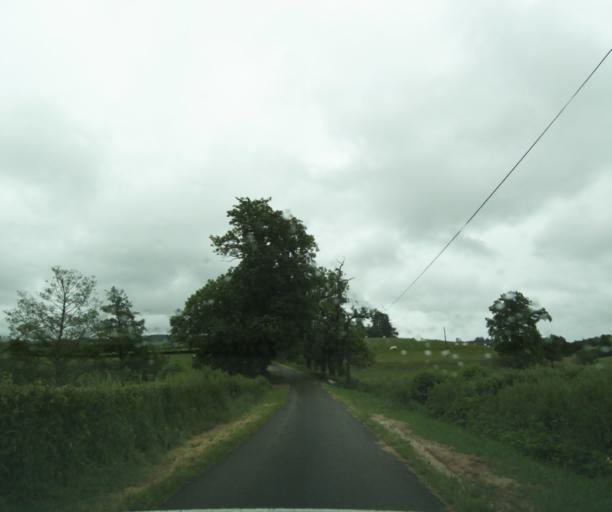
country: FR
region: Bourgogne
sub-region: Departement de Saone-et-Loire
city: Saint-Vallier
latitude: 46.4945
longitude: 4.4553
